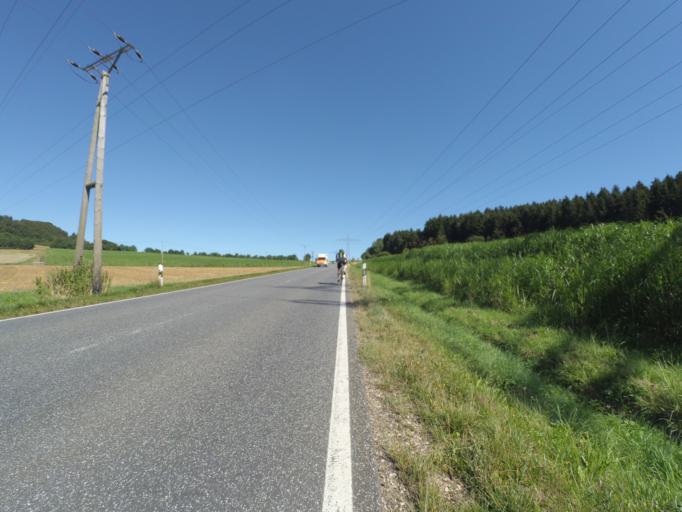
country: DE
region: Rheinland-Pfalz
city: Berlingen
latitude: 50.2308
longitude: 6.7229
